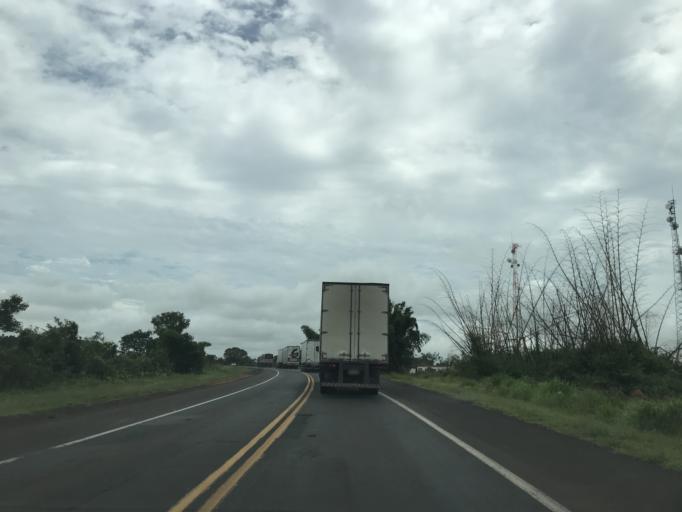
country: BR
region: Minas Gerais
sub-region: Frutal
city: Frutal
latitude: -19.8567
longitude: -48.9624
